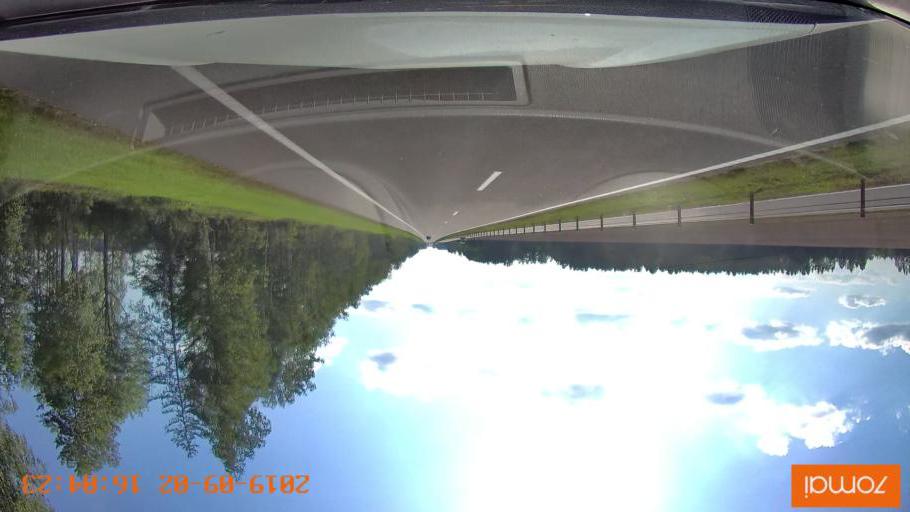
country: BY
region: Minsk
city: Byerazino
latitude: 53.7984
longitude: 28.8468
